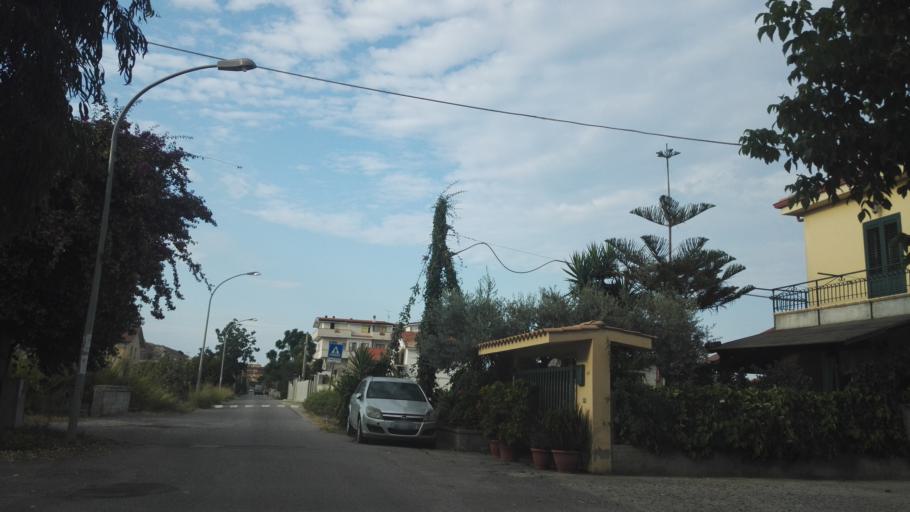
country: IT
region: Calabria
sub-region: Provincia di Reggio Calabria
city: Monasterace Marina
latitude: 38.4295
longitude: 16.5684
